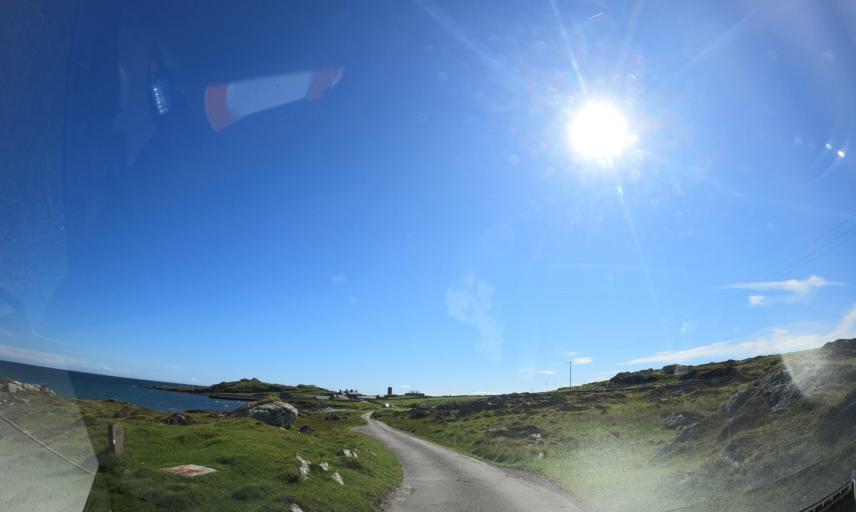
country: GB
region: Scotland
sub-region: Eilean Siar
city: Barra
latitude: 56.4523
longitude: -6.8957
